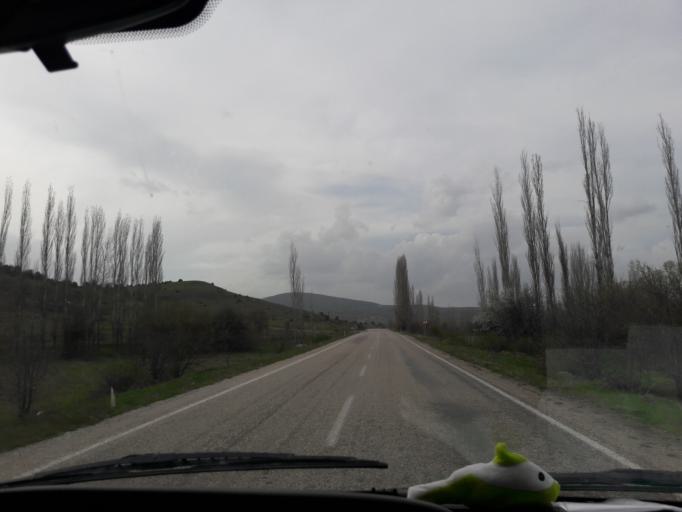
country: TR
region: Gumushane
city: Siran
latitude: 40.1664
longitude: 39.0059
